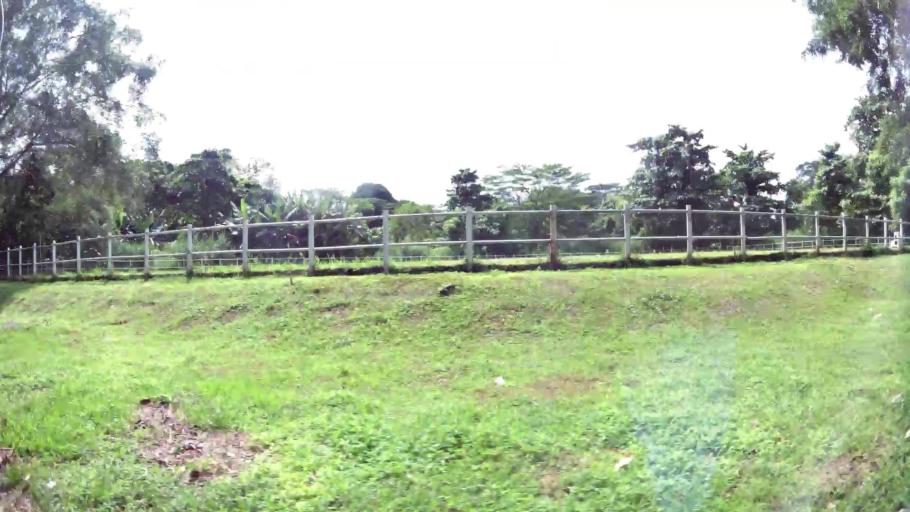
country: SG
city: Singapore
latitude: 1.3361
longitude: 103.7974
